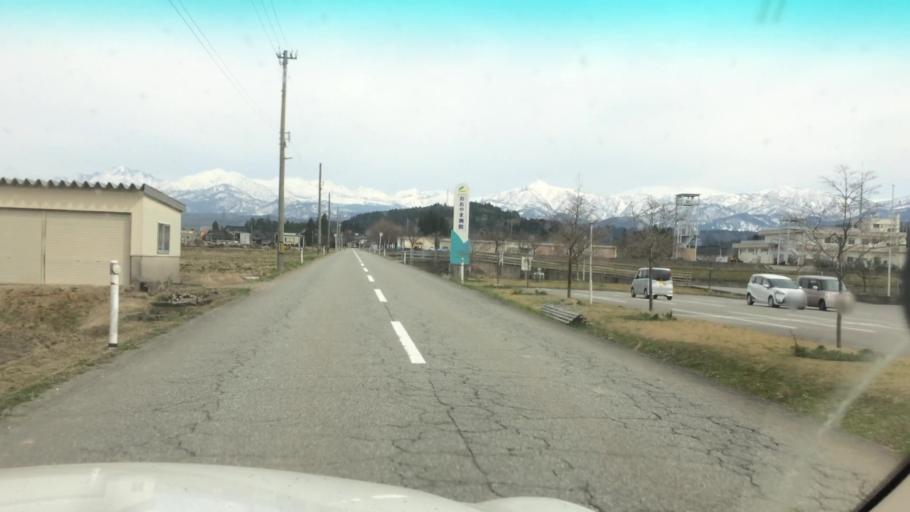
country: JP
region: Toyama
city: Toyama-shi
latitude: 36.6104
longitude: 137.2806
